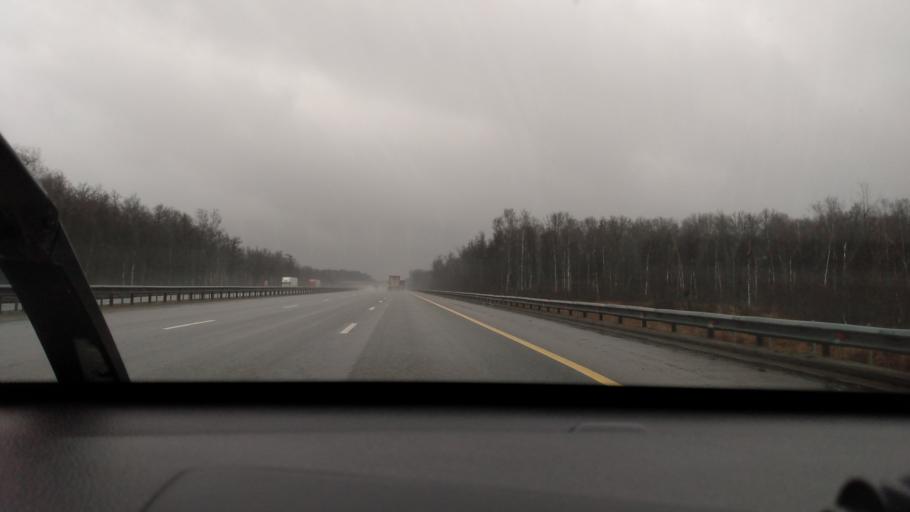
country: RU
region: Moskovskaya
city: Stupino
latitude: 54.9015
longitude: 38.0112
